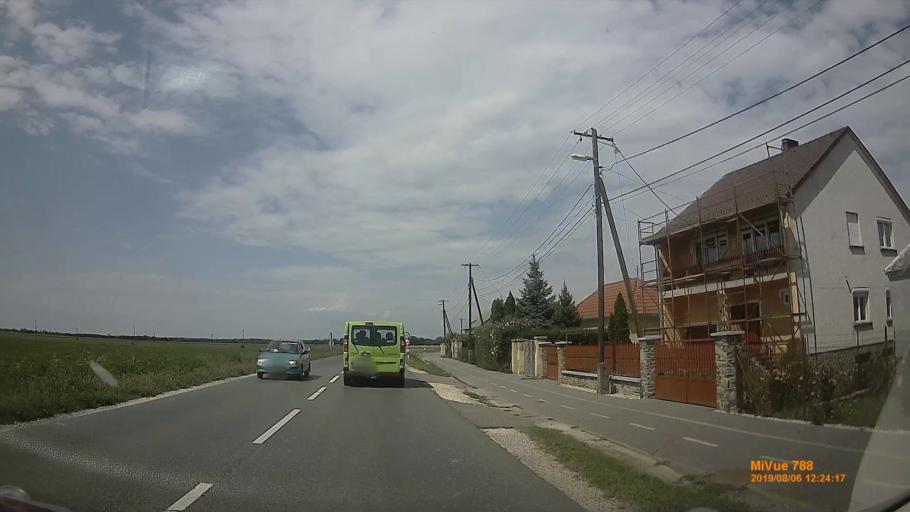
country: HU
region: Vas
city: Taplanszentkereszt
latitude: 47.1921
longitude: 16.7001
